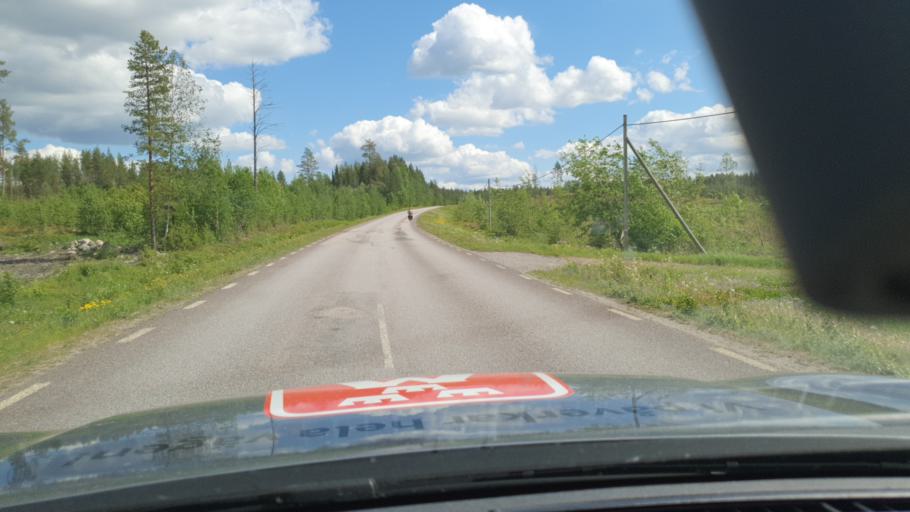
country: SE
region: Norrbotten
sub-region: Pitea Kommun
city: Norrfjarden
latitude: 65.5147
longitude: 21.5244
